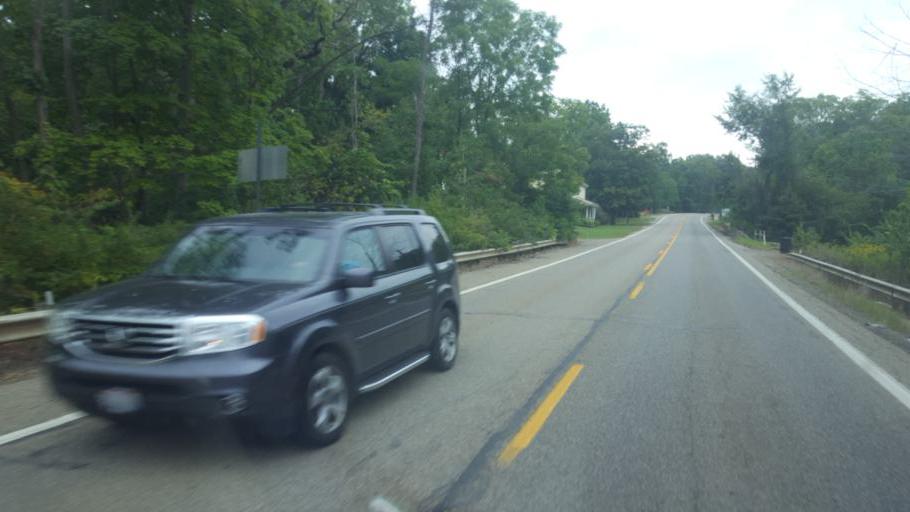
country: US
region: Ohio
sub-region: Morrow County
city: Mount Gilead
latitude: 40.5486
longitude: -82.8206
